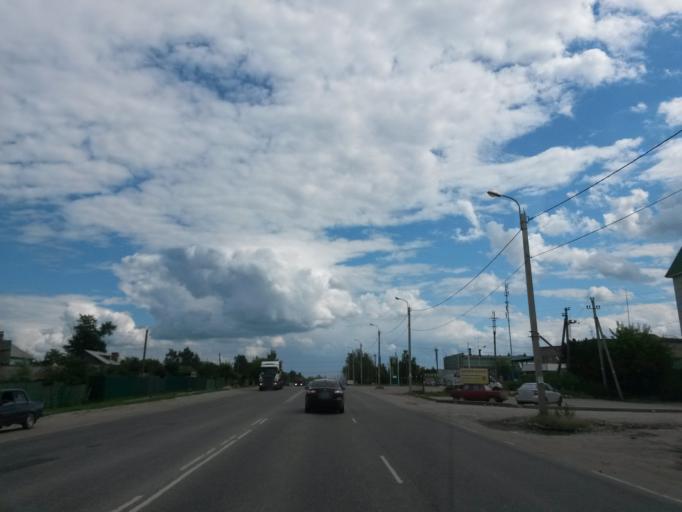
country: RU
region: Ivanovo
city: Novo-Talitsy
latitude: 57.0072
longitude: 40.8670
